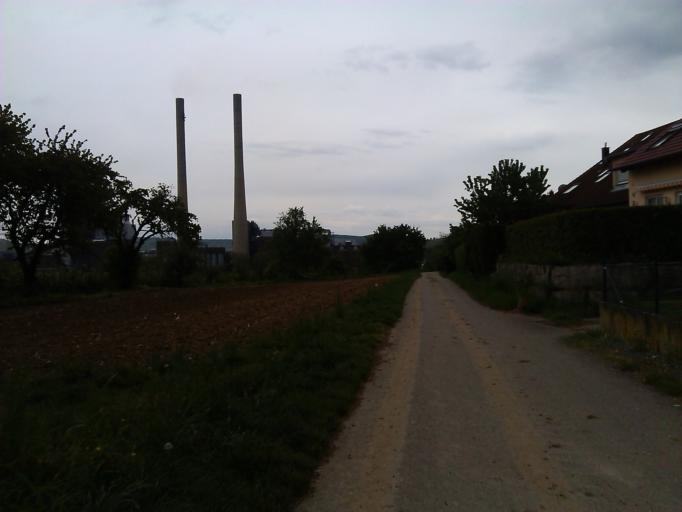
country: DE
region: Baden-Wuerttemberg
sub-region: Regierungsbezirk Stuttgart
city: Neckarsulm
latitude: 49.1731
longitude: 9.1952
